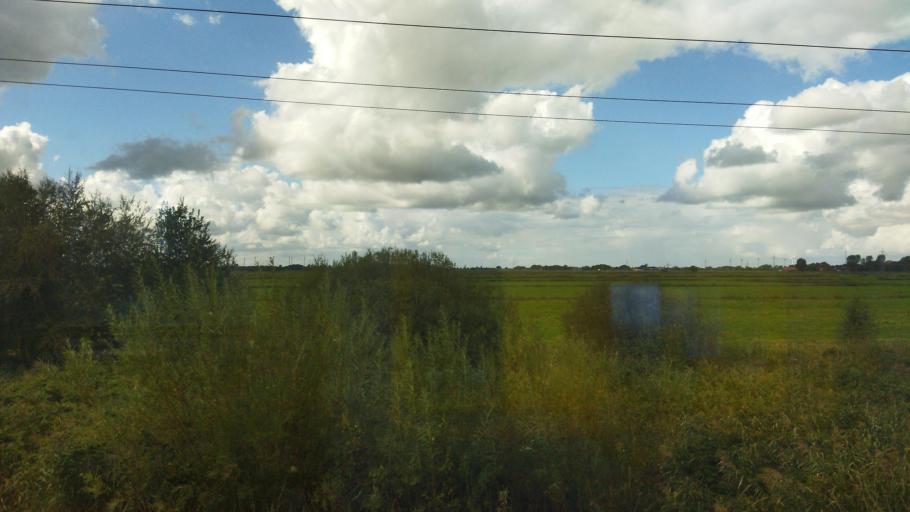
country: DE
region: Lower Saxony
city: Leer
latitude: 53.2022
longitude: 7.4653
